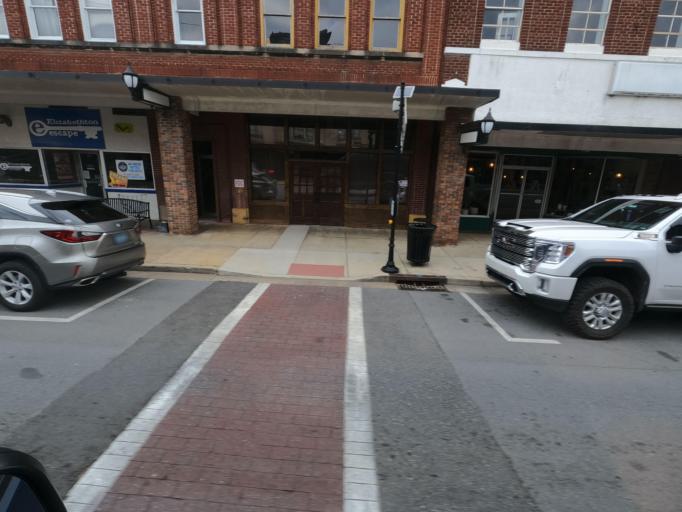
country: US
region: Tennessee
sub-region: Carter County
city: Elizabethton
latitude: 36.3478
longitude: -82.2155
